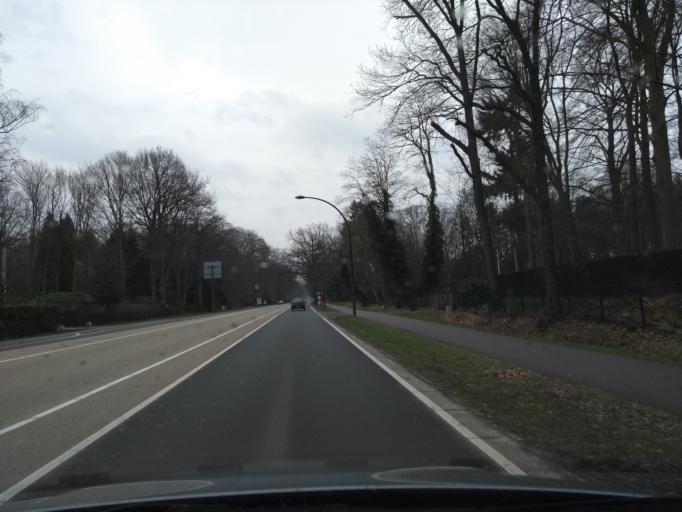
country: NL
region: Overijssel
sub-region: Gemeente Hengelo
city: Hengelo
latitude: 52.2562
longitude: 6.8125
